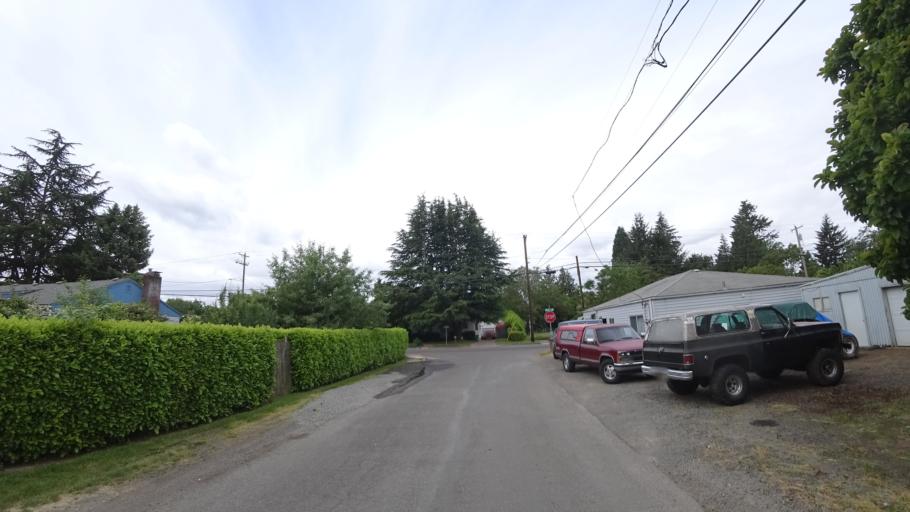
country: US
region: Oregon
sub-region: Multnomah County
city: Lents
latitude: 45.4937
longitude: -122.5680
